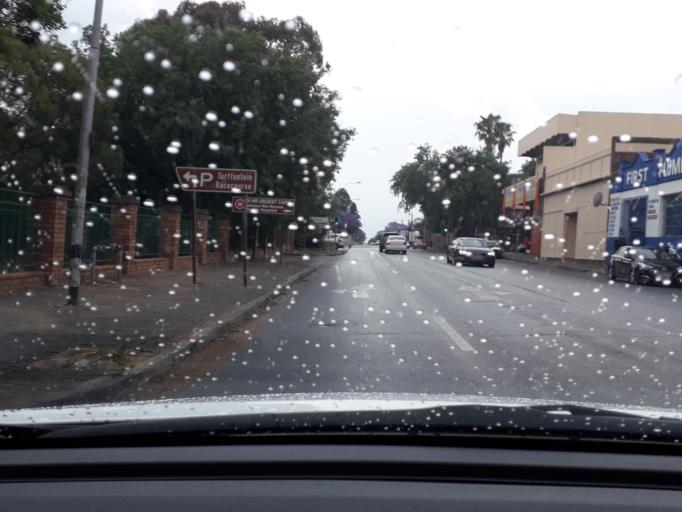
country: ZA
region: Gauteng
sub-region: City of Johannesburg Metropolitan Municipality
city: Johannesburg
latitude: -26.2400
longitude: 28.0383
